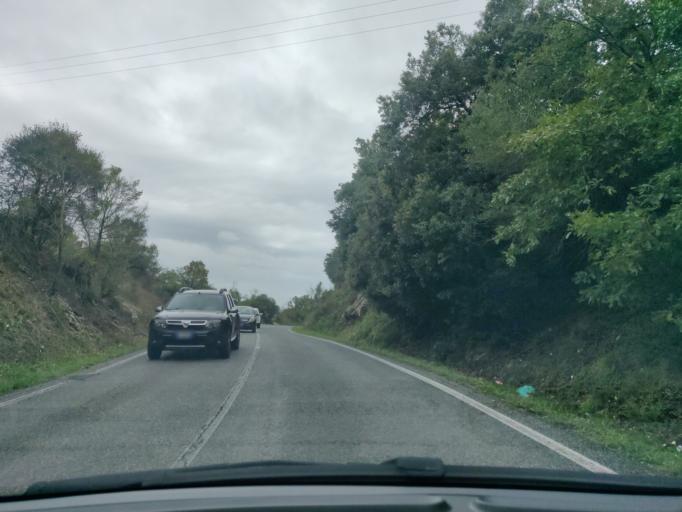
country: IT
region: Latium
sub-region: Citta metropolitana di Roma Capitale
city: Allumiere
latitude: 42.1379
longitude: 11.8714
